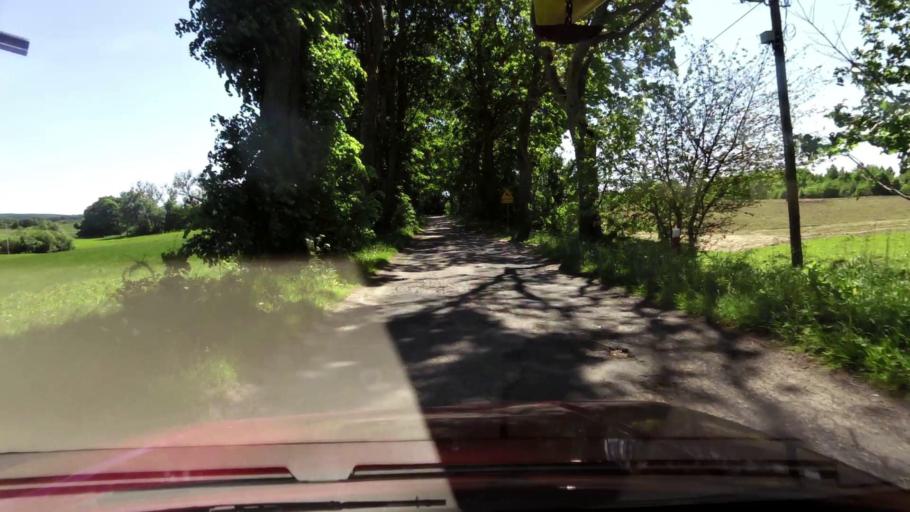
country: PL
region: West Pomeranian Voivodeship
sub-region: Powiat koszalinski
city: Bobolice
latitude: 54.0155
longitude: 16.6528
